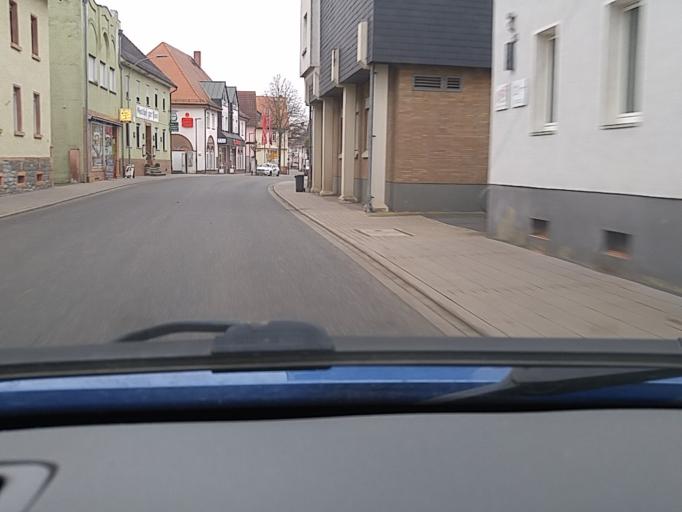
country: DE
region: Hesse
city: Reichelsheim
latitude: 50.3588
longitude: 8.8752
